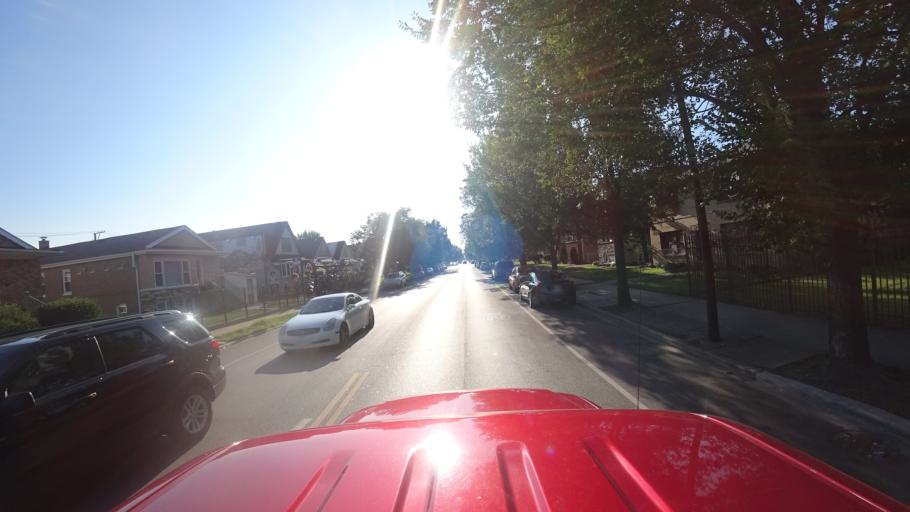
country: US
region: Illinois
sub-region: Cook County
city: Hometown
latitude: 41.7859
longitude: -87.7223
